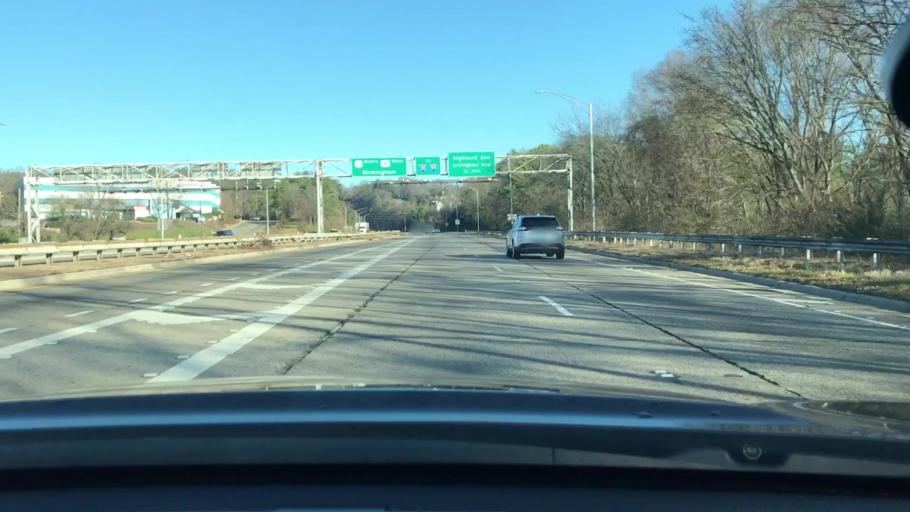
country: US
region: Alabama
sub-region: Jefferson County
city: Homewood
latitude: 33.4870
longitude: -86.7867
